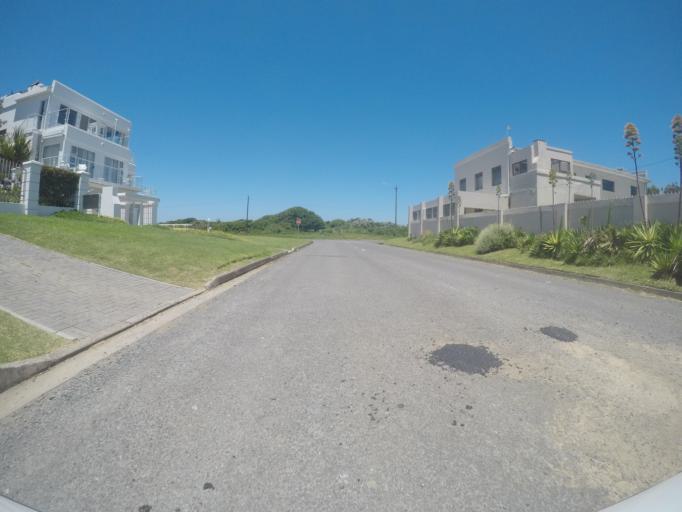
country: ZA
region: Eastern Cape
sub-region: Buffalo City Metropolitan Municipality
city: East London
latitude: -32.9506
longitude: 28.0150
